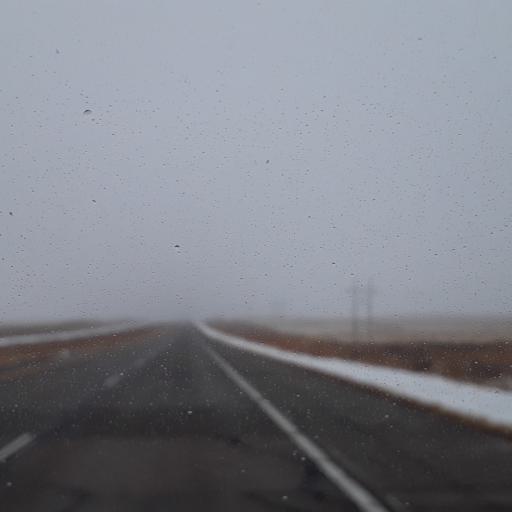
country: US
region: Colorado
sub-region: Logan County
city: Sterling
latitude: 40.7812
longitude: -102.9131
